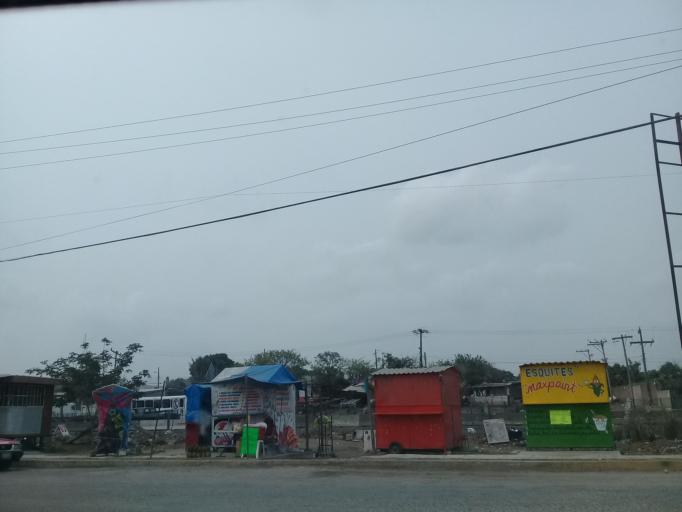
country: MX
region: Veracruz
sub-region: Veracruz
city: Colonia Chalchihuecan
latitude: 19.2160
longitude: -96.2127
